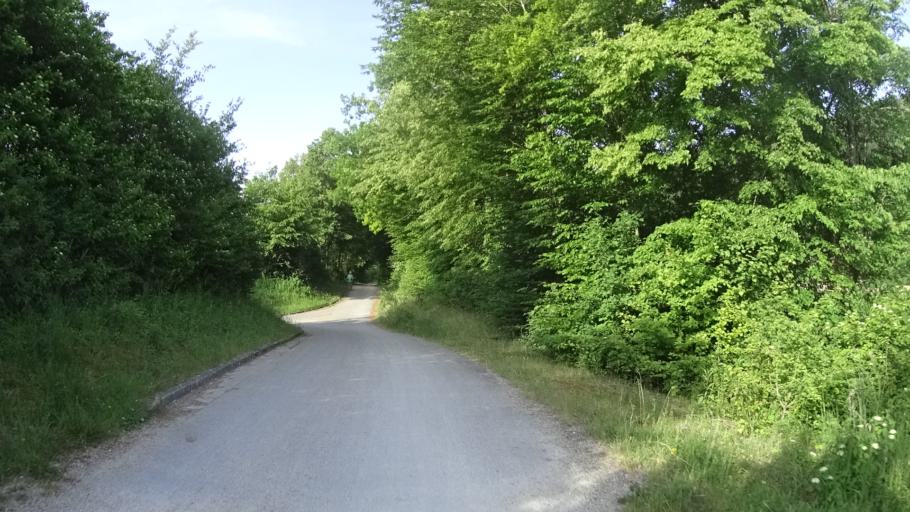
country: DE
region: Bavaria
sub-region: Lower Bavaria
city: Riedenburg
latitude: 48.9714
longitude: 11.6853
